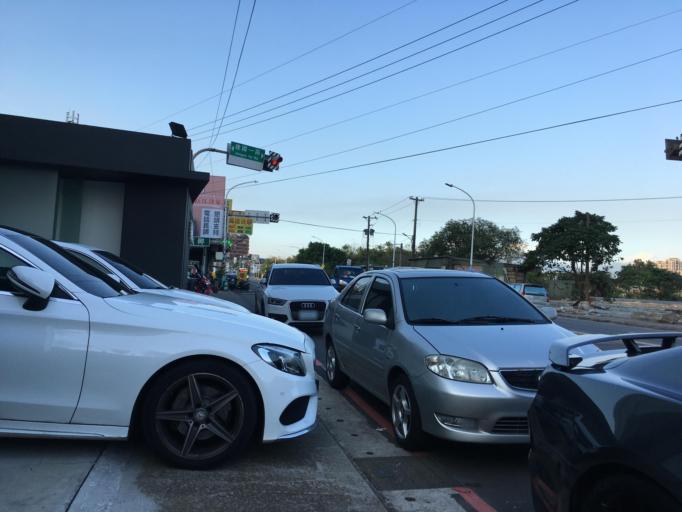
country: TW
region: Taipei
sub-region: Taipei
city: Banqiao
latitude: 25.0245
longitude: 121.4349
